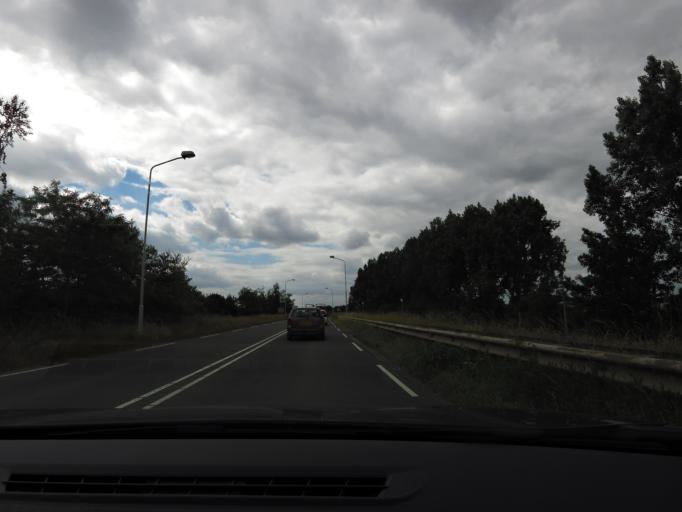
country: NL
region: North Brabant
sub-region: Gemeente Oosterhout
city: Oosterhout
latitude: 51.6553
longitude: 4.8512
